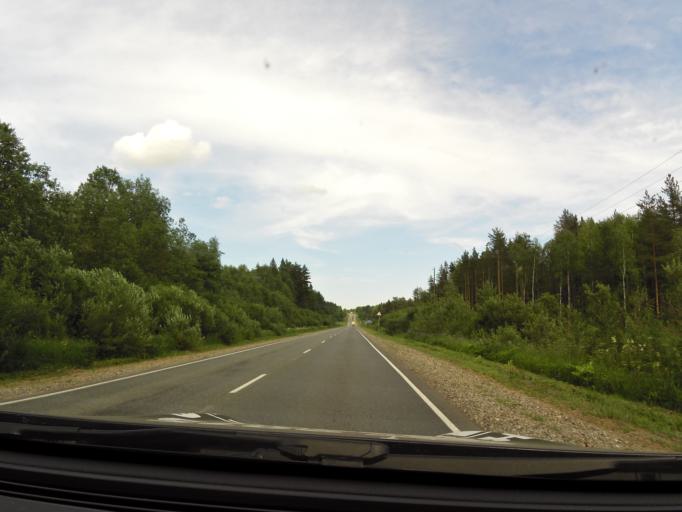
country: RU
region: Kirov
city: Slobodskoy
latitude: 58.7303
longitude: 50.2651
